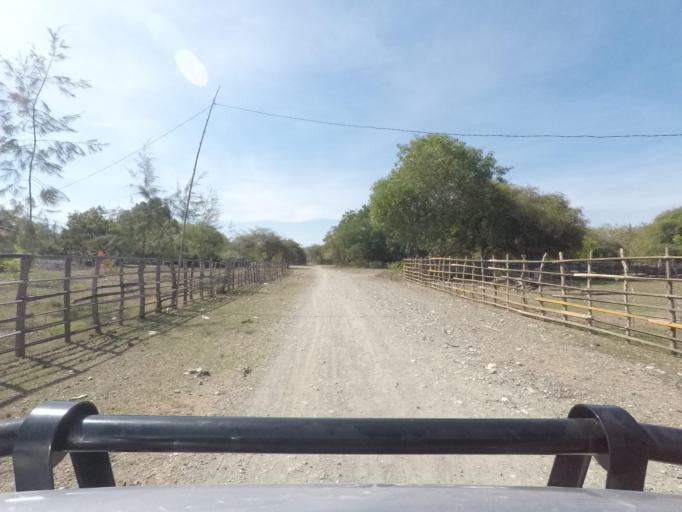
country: TL
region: Bobonaro
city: Maliana
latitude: -8.8887
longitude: 125.0040
